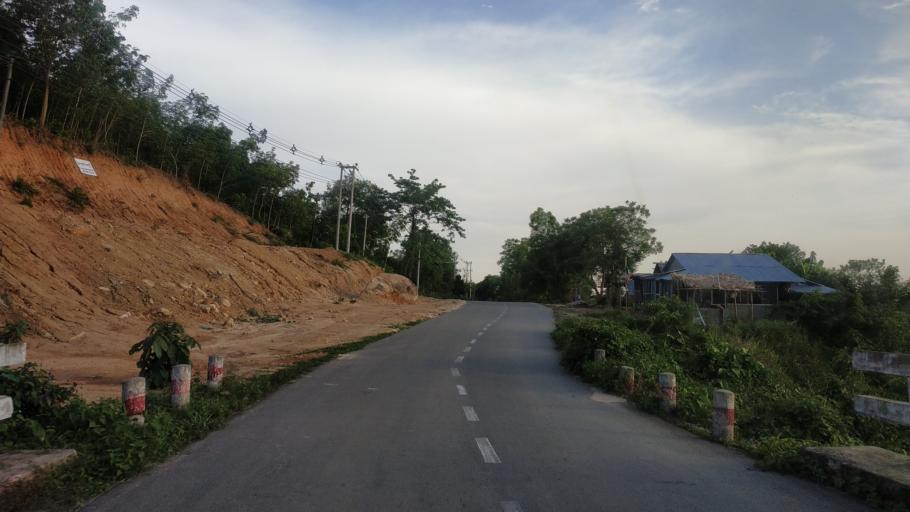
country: MM
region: Mon
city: Kyaikto
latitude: 17.4188
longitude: 97.0712
